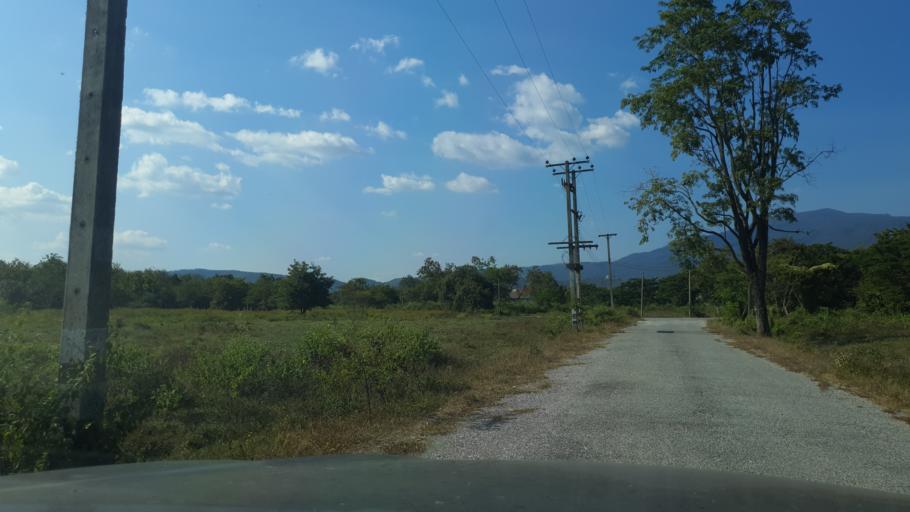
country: TH
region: Chiang Mai
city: Hang Dong
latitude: 18.7359
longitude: 98.9440
